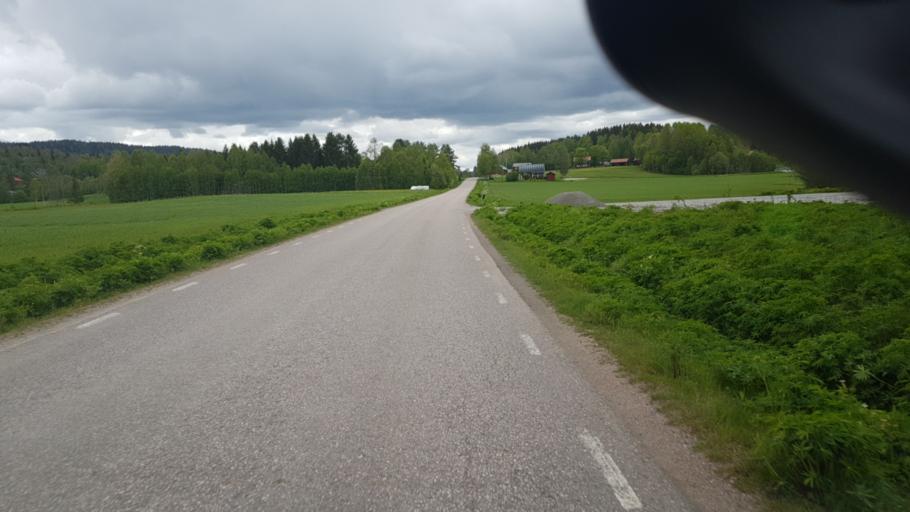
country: SE
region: Vaermland
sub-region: Arvika Kommun
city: Arvika
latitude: 59.7491
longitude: 12.8022
